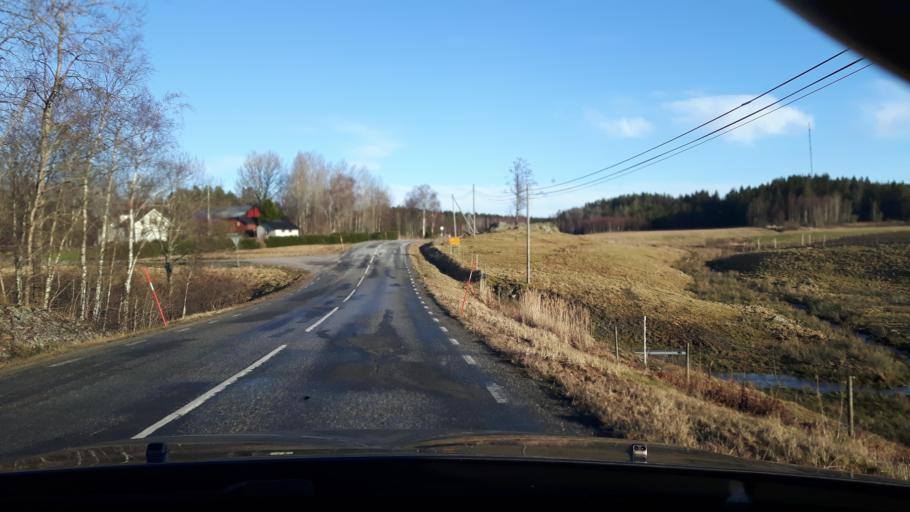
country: SE
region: Vaestra Goetaland
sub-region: Munkedals Kommun
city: Munkedal
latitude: 58.5434
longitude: 11.7024
